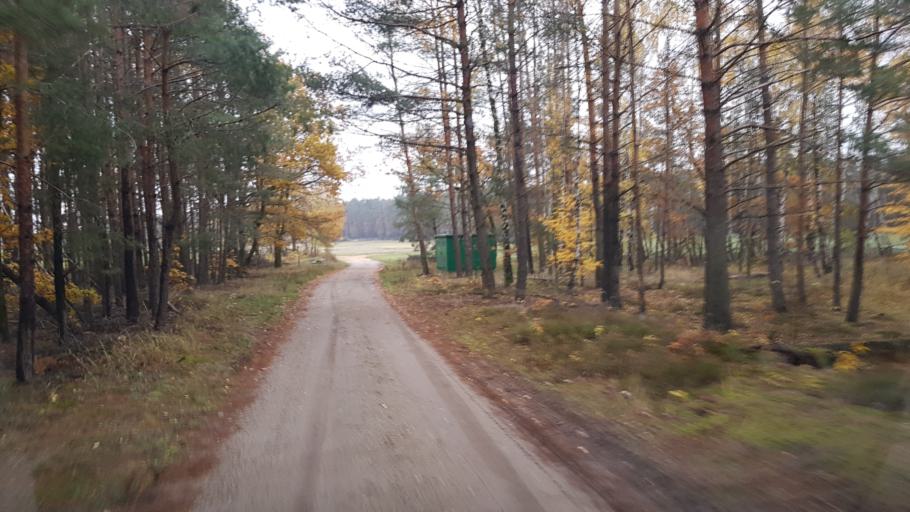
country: DE
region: Brandenburg
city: Schilda
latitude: 51.6397
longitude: 13.3973
